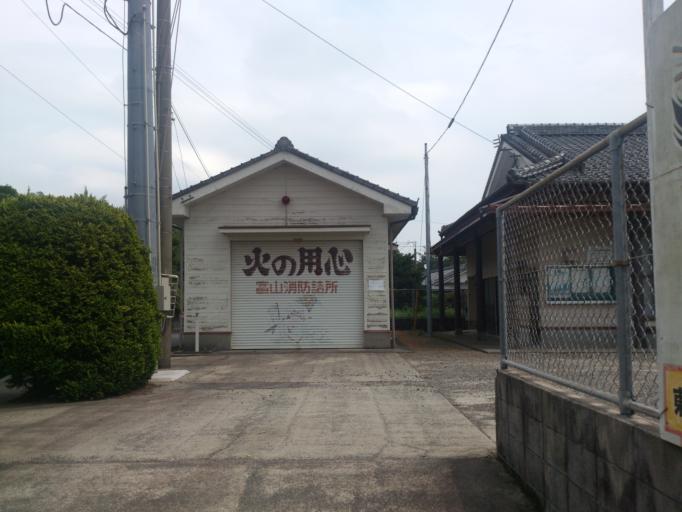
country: JP
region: Kagoshima
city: Kanoya
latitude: 31.3794
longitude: 130.9016
